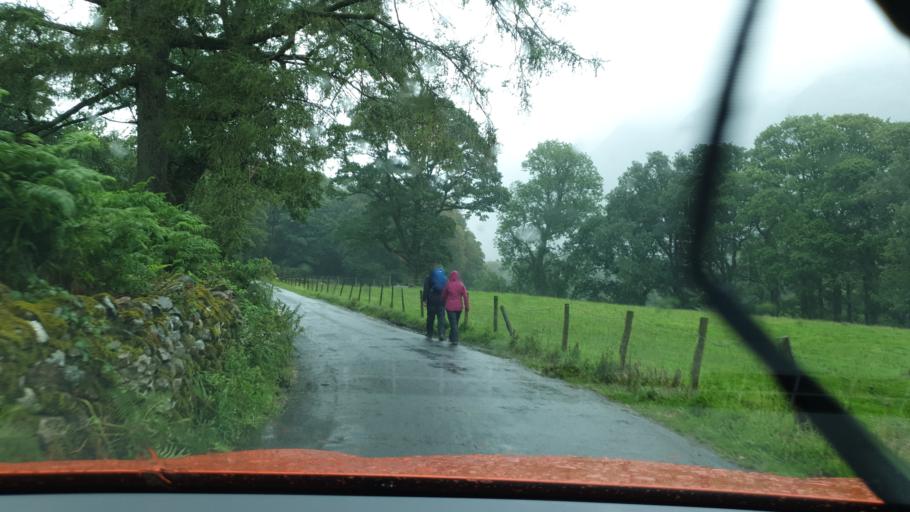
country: GB
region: England
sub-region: Cumbria
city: Seascale
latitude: 54.4251
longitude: -3.3281
